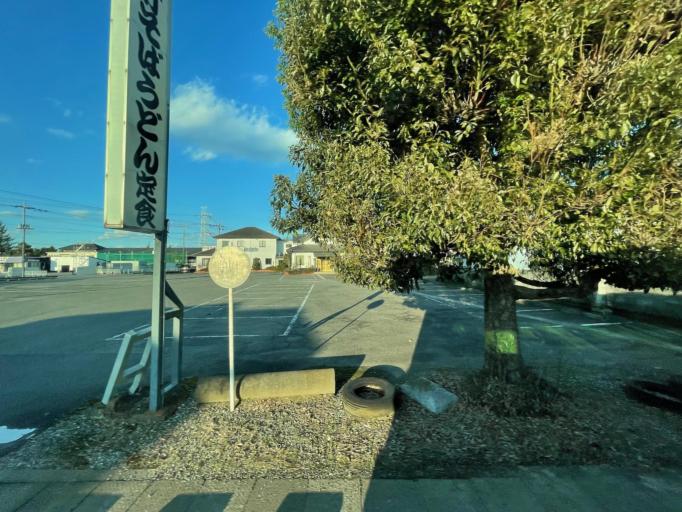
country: JP
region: Saitama
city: Satte
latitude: 36.0714
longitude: 139.7620
